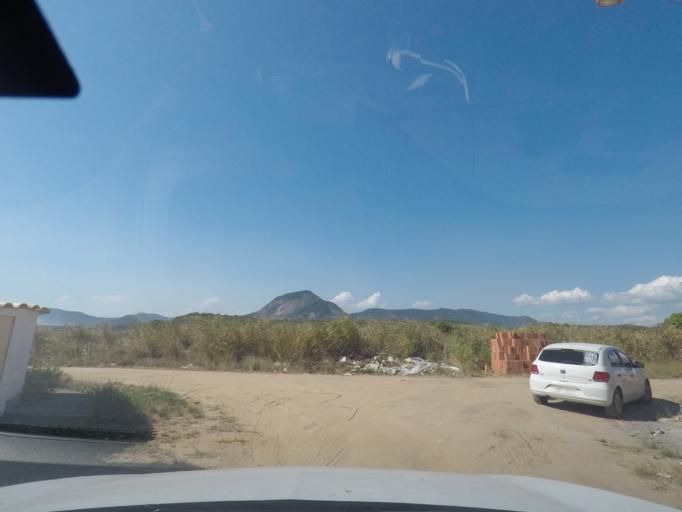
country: BR
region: Rio de Janeiro
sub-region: Marica
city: Marica
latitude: -22.9646
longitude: -42.9056
